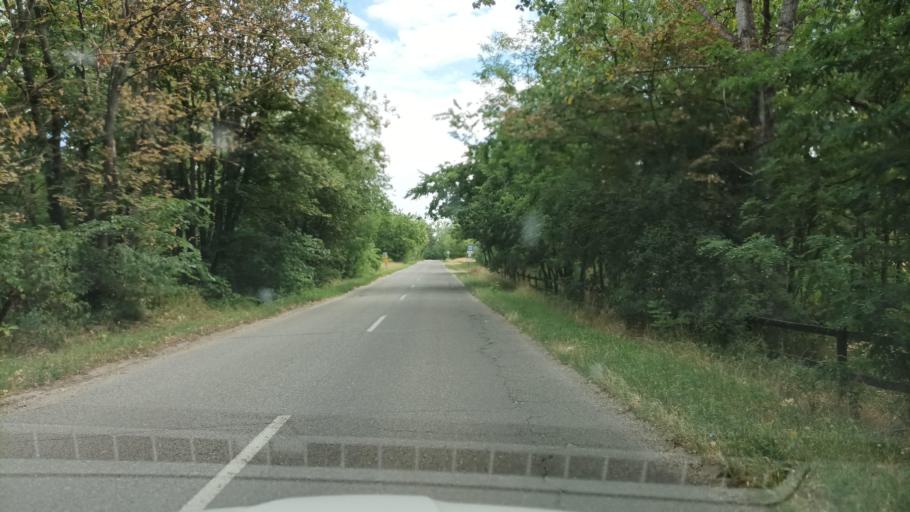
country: HU
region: Pest
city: Tahitotfalu
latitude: 47.7693
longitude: 19.1125
